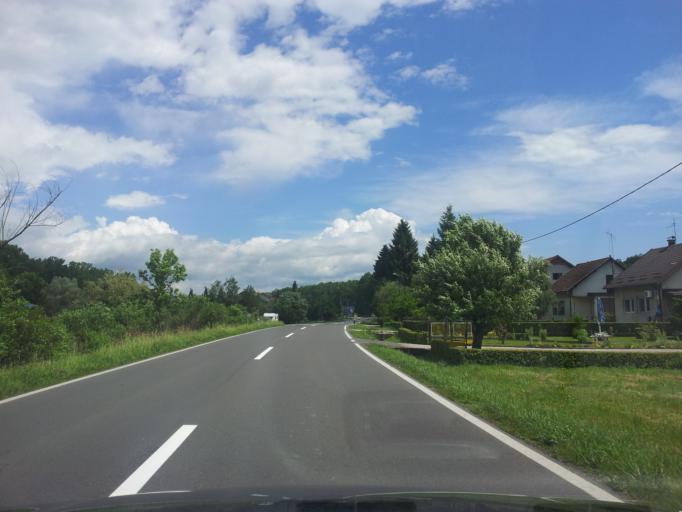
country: HR
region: Karlovacka
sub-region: Grad Karlovac
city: Karlovac
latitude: 45.5323
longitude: 15.5666
